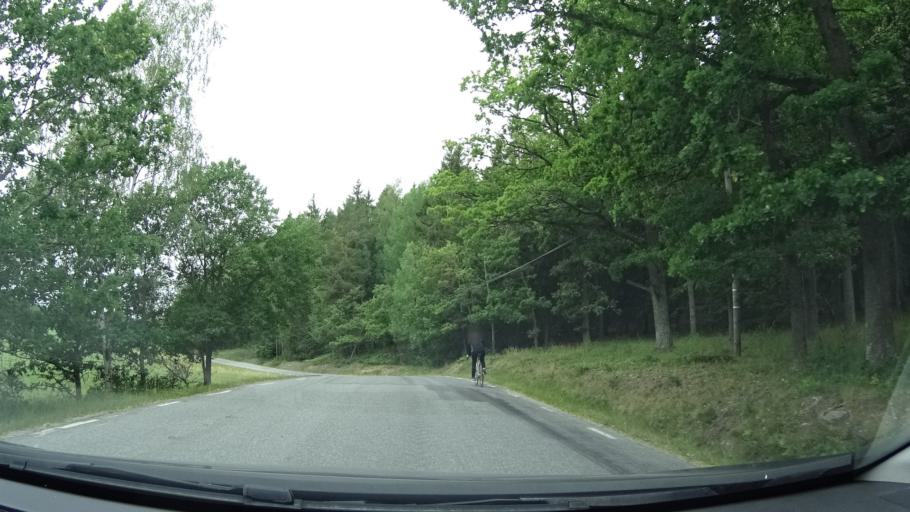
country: SE
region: Stockholm
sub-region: Varmdo Kommun
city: Mortnas
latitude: 59.3648
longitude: 18.4737
